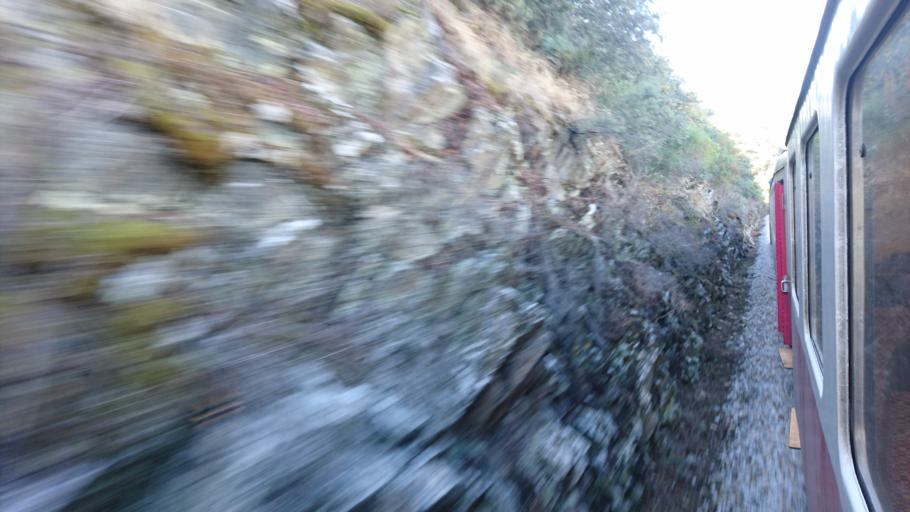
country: PT
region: Guarda
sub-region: Vila Nova de Foz Coa
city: Vila Nova de Foz Coa
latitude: 41.1344
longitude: -7.2136
